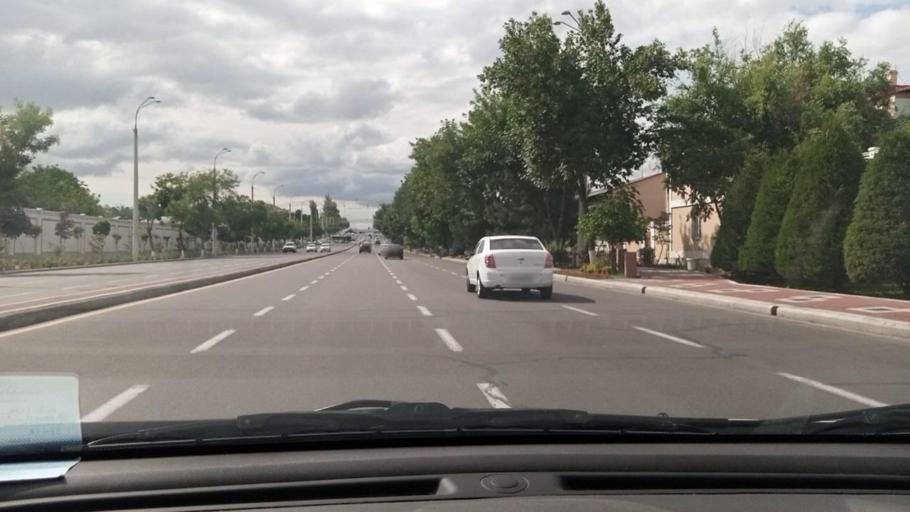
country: UZ
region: Toshkent
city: Salor
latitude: 41.3273
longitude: 69.3577
